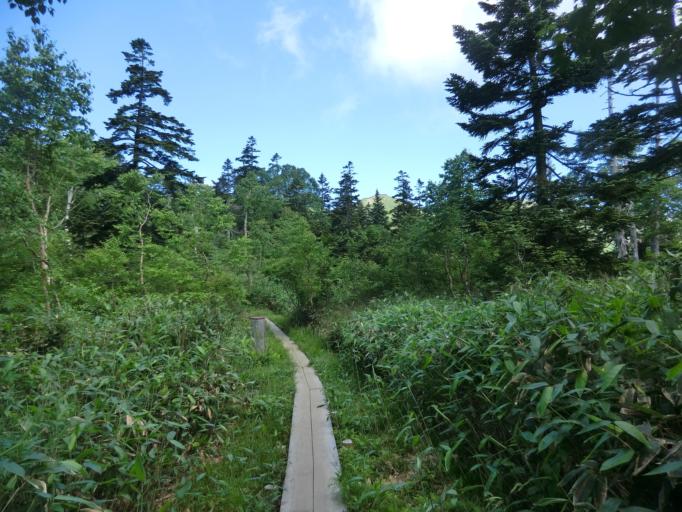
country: JP
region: Gunma
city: Numata
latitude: 36.8843
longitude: 139.1823
